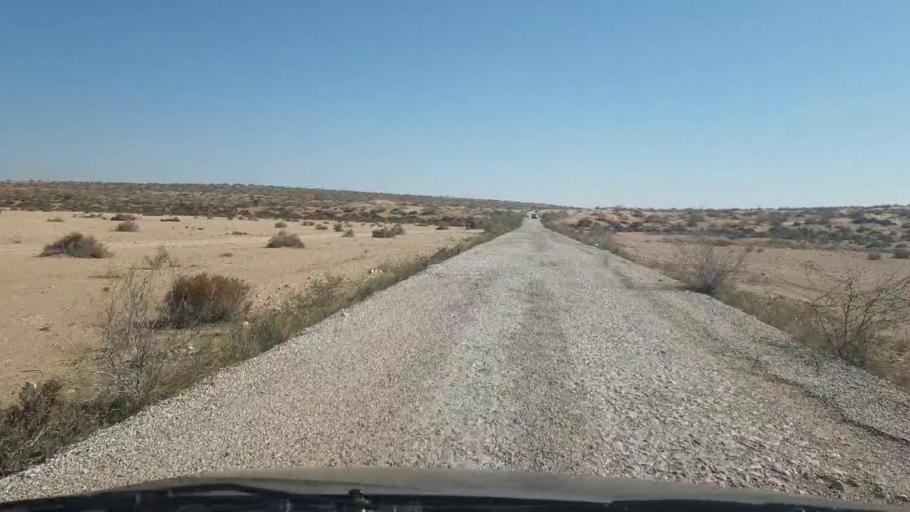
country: PK
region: Sindh
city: Bozdar
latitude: 27.0196
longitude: 68.7274
